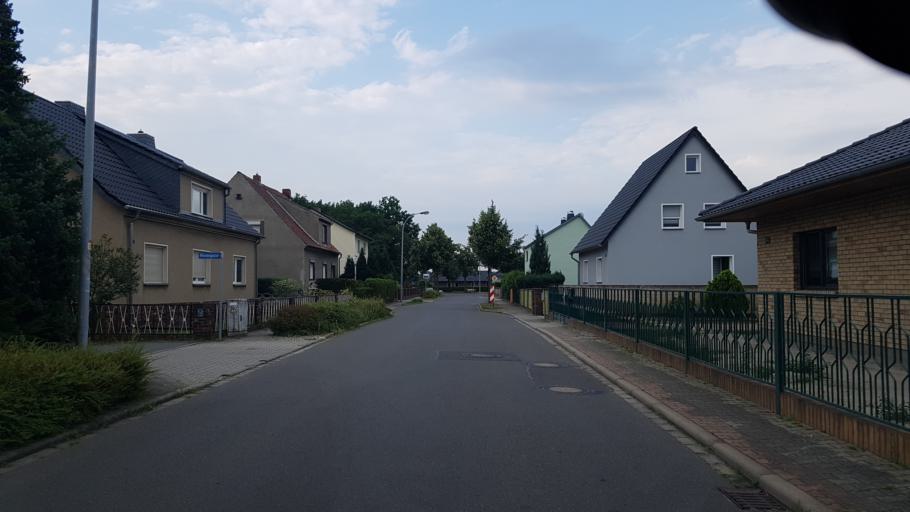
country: DE
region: Brandenburg
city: Tettau
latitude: 51.4251
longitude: 13.7279
